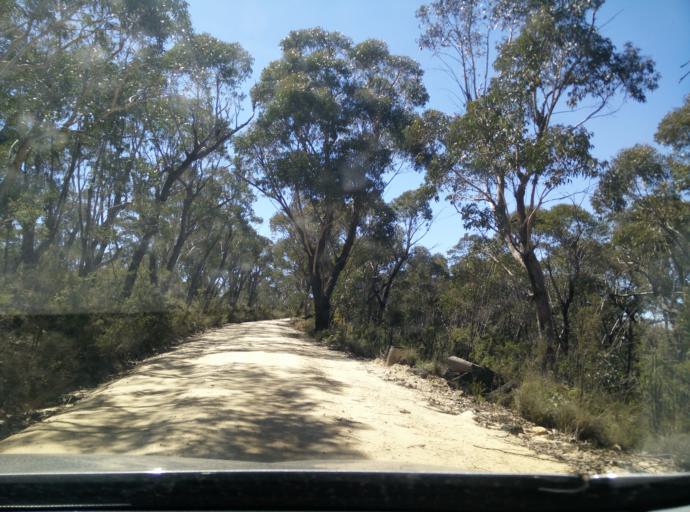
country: AU
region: New South Wales
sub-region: Blue Mountains Municipality
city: Blackheath
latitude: -33.5881
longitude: 150.2701
